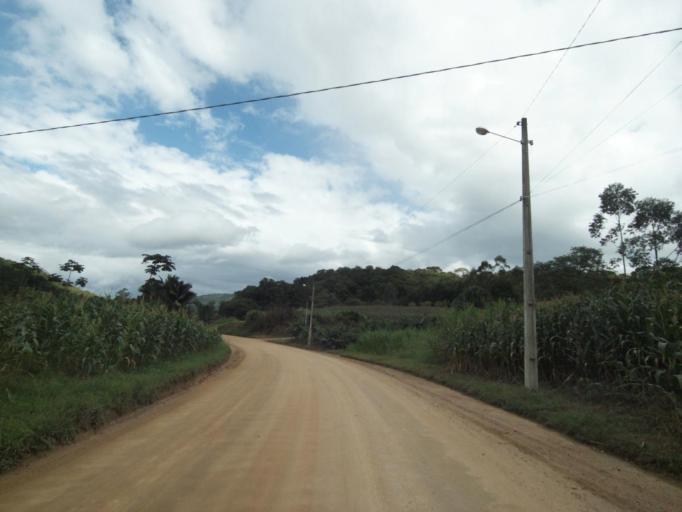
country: BR
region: Santa Catarina
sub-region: Pomerode
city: Pomerode
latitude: -26.7105
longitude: -49.2101
